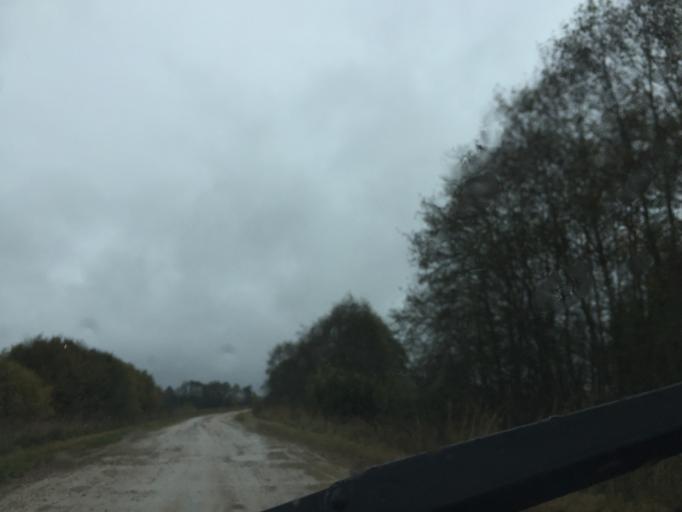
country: LV
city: Tireli
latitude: 56.7727
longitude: 23.5439
